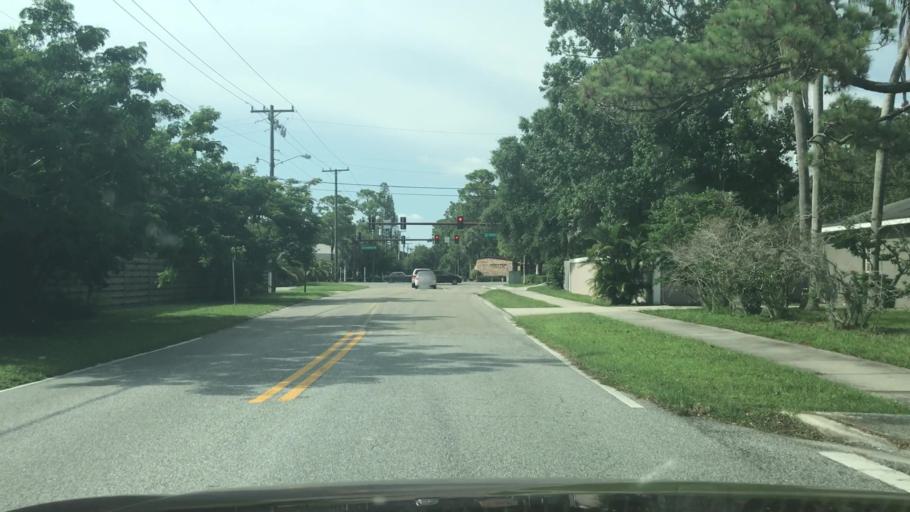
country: US
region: Florida
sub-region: Sarasota County
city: Sarasota
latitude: 27.3365
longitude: -82.5222
